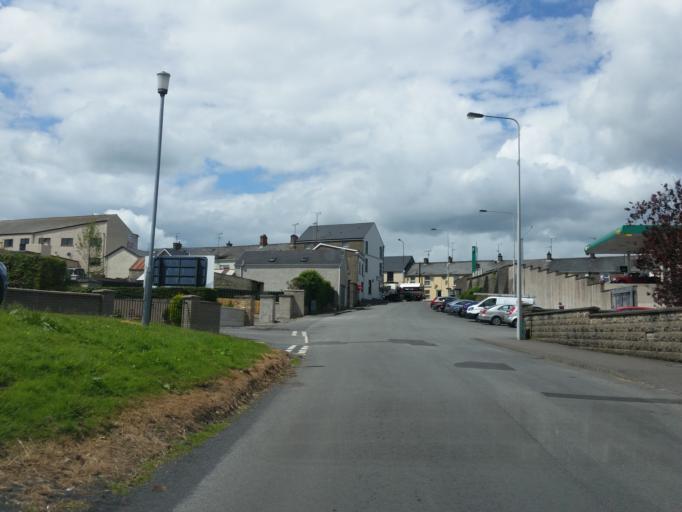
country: GB
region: Northern Ireland
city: Fivemiletown
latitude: 54.3778
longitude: -7.3128
